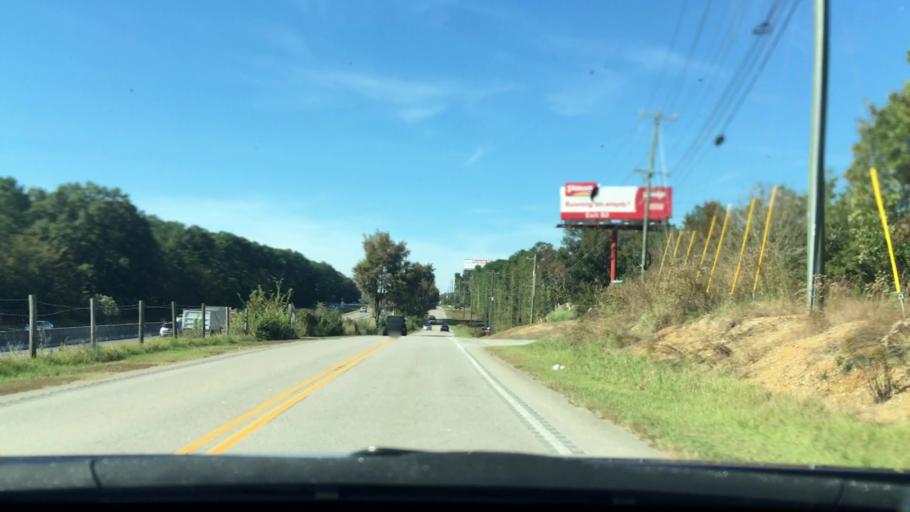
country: US
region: South Carolina
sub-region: Lexington County
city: Irmo
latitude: 34.1046
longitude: -81.1802
